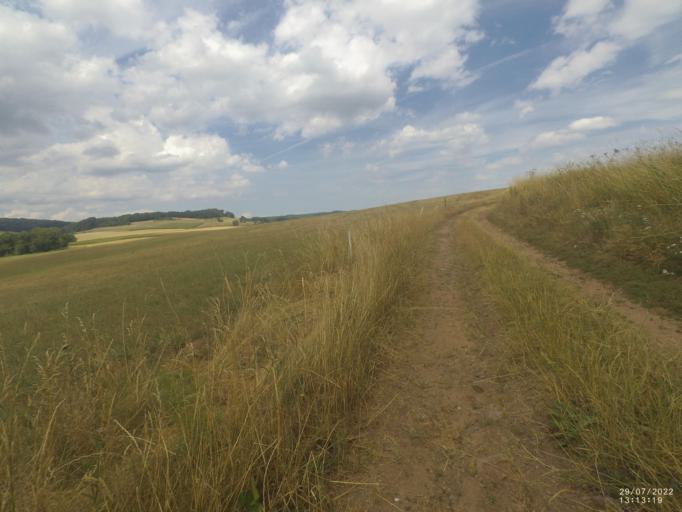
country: DE
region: Rheinland-Pfalz
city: Steffeln
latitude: 50.2769
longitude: 6.5772
